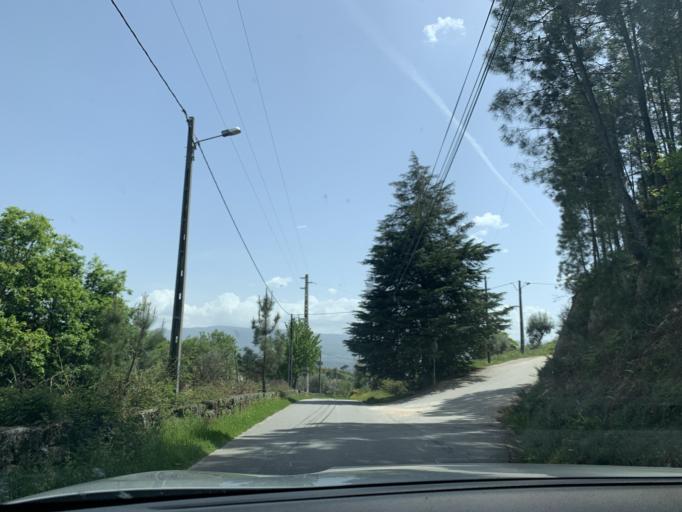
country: PT
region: Guarda
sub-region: Fornos de Algodres
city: Fornos de Algodres
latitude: 40.5926
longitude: -7.6293
